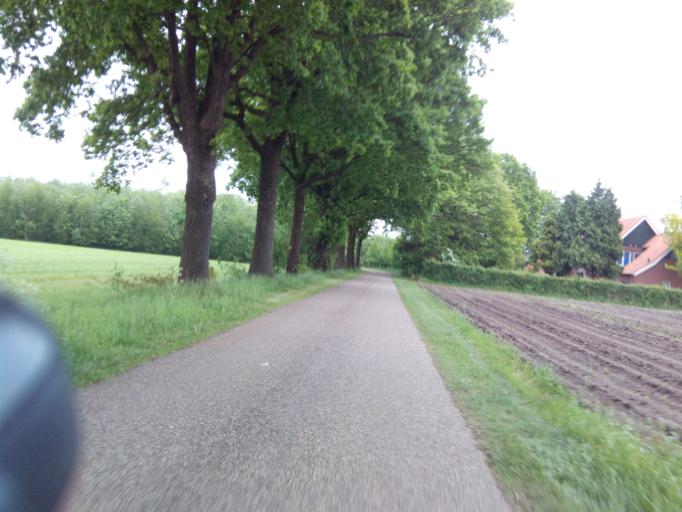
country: NL
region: Gelderland
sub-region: Berkelland
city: Neede
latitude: 52.0778
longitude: 6.5859
